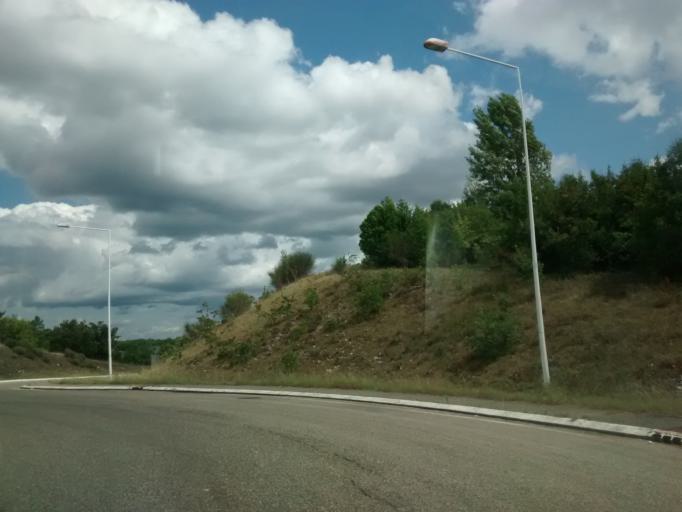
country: FR
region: Midi-Pyrenees
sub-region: Departement du Lot
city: Lalbenque
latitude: 44.3445
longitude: 1.4736
